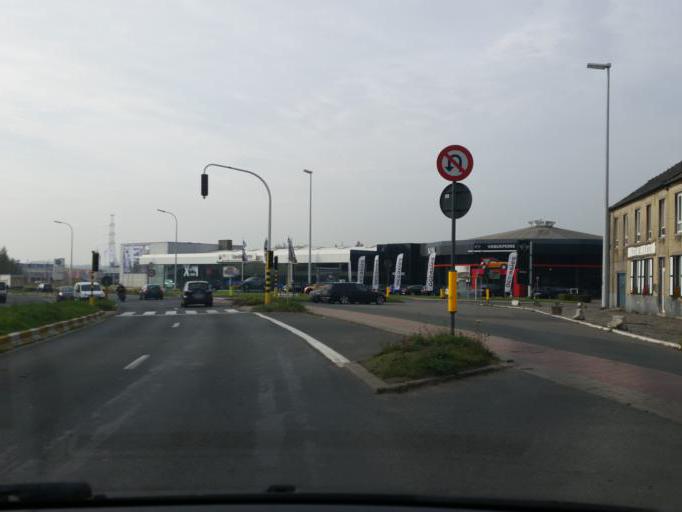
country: BE
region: Flanders
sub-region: Provincie Vlaams-Brabant
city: Sint-Pieters-Leeuw
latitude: 50.7654
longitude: 4.2519
